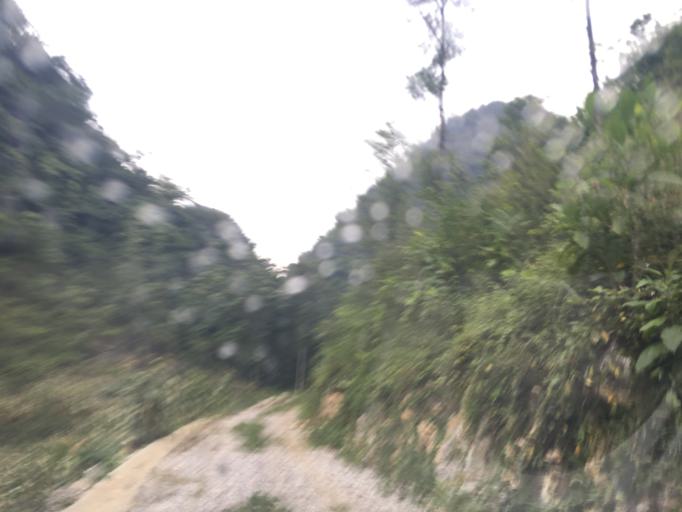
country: CN
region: Guangxi Zhuangzu Zizhiqu
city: Xinzhou
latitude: 25.2263
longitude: 105.6279
